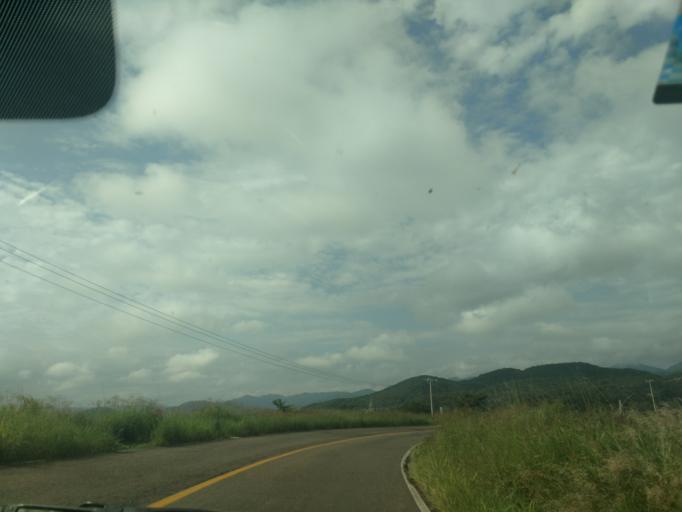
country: MX
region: Jalisco
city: El Salto
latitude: 20.3843
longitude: -104.5355
